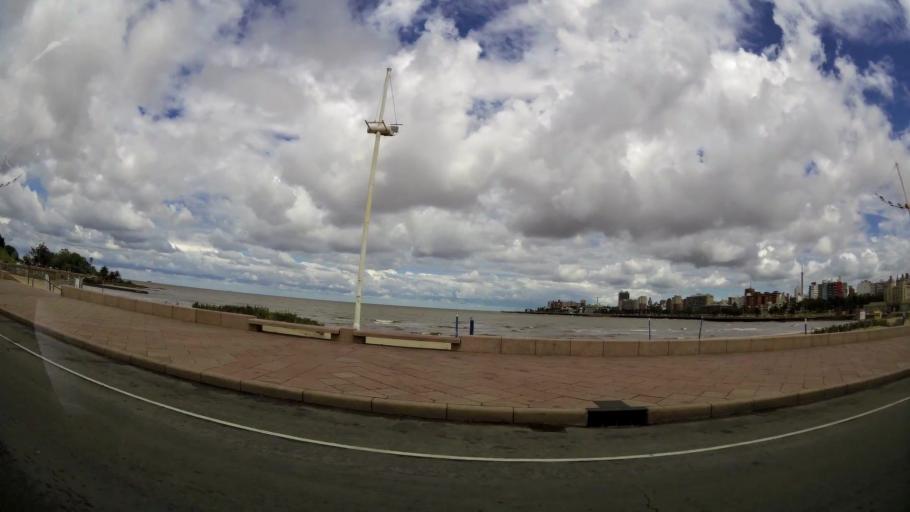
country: UY
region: Montevideo
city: Montevideo
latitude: -34.9173
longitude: -56.1691
